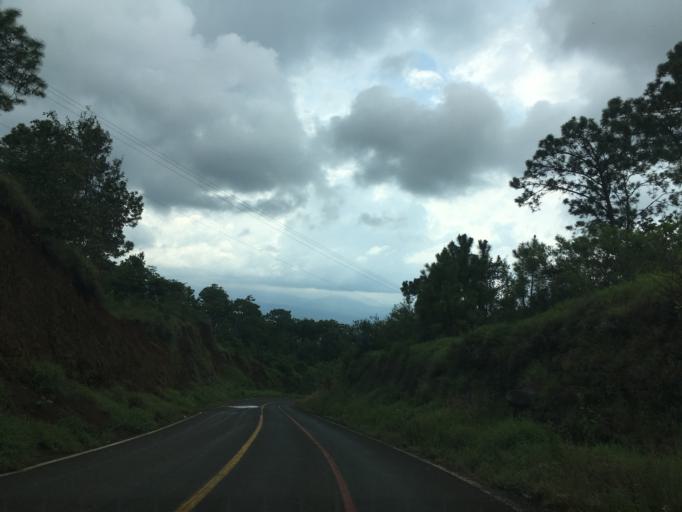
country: MX
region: Michoacan
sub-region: Periban
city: San Francisco Periban
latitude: 19.6048
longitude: -102.4038
